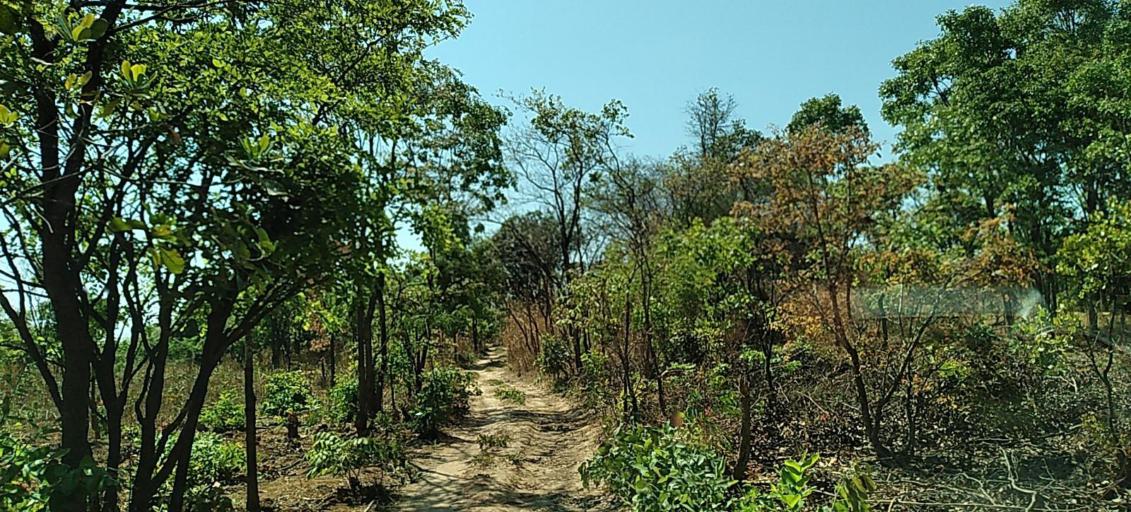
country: ZM
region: Copperbelt
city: Chililabombwe
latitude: -12.2883
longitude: 27.8881
